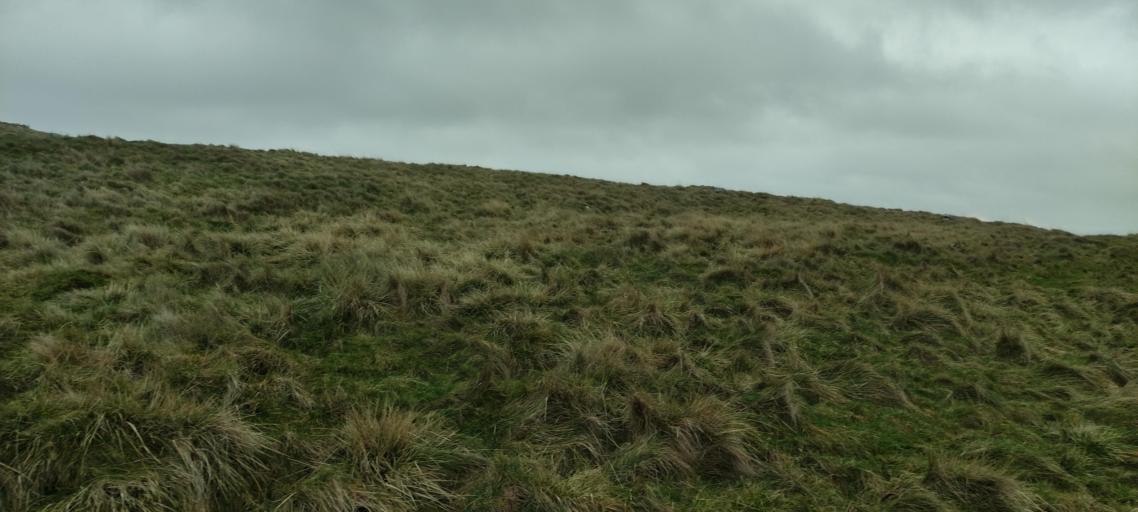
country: GB
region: England
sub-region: North Yorkshire
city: Gargrave
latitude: 54.0716
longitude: -2.1381
